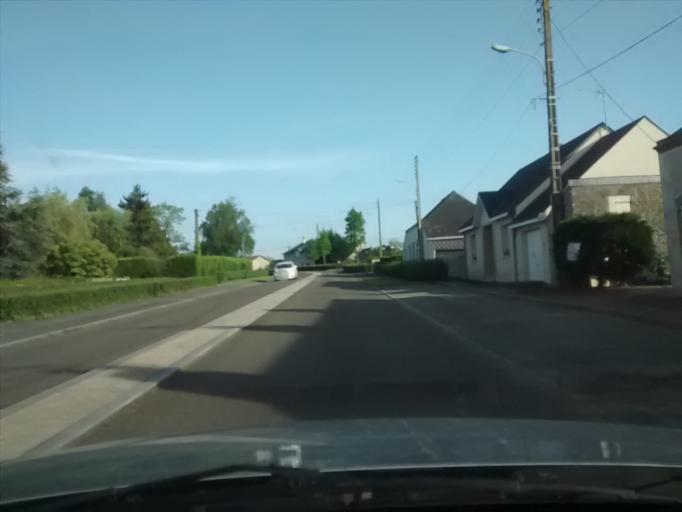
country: FR
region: Pays de la Loire
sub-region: Departement de la Mayenne
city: Vaiges
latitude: 48.0384
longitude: -0.4751
